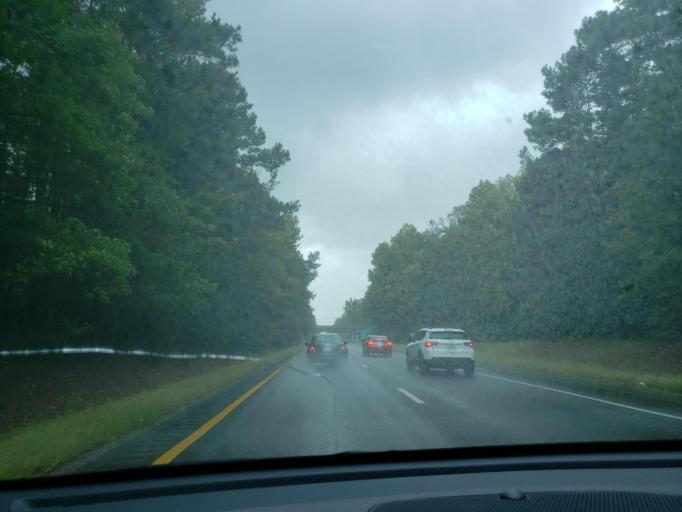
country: US
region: Virginia
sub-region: Mecklenburg County
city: South Hill
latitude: 36.7154
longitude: -78.1127
